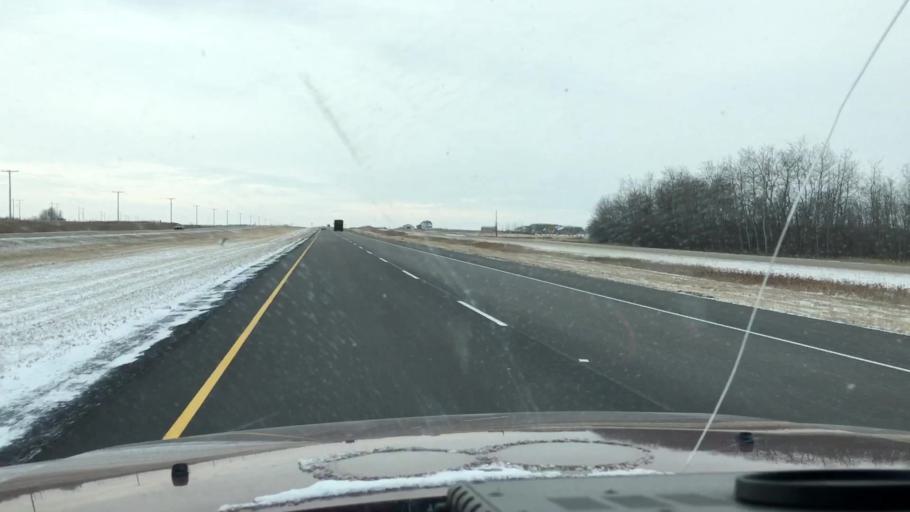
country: CA
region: Saskatchewan
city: Saskatoon
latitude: 51.9357
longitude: -106.5379
